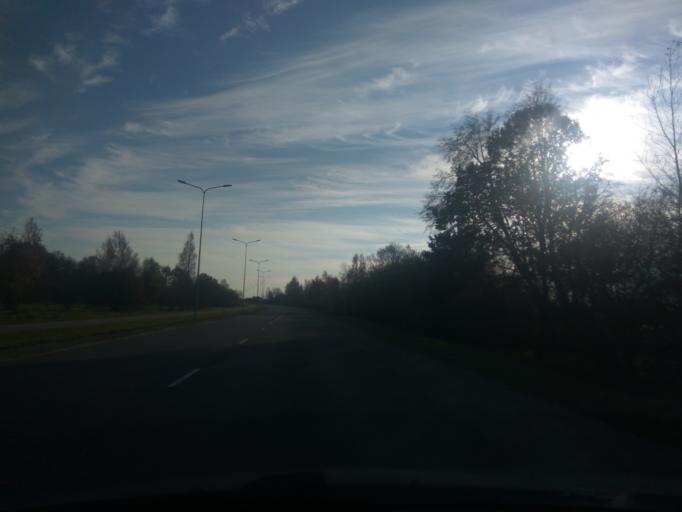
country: LV
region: Ventspils
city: Ventspils
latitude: 57.3631
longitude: 21.5632
